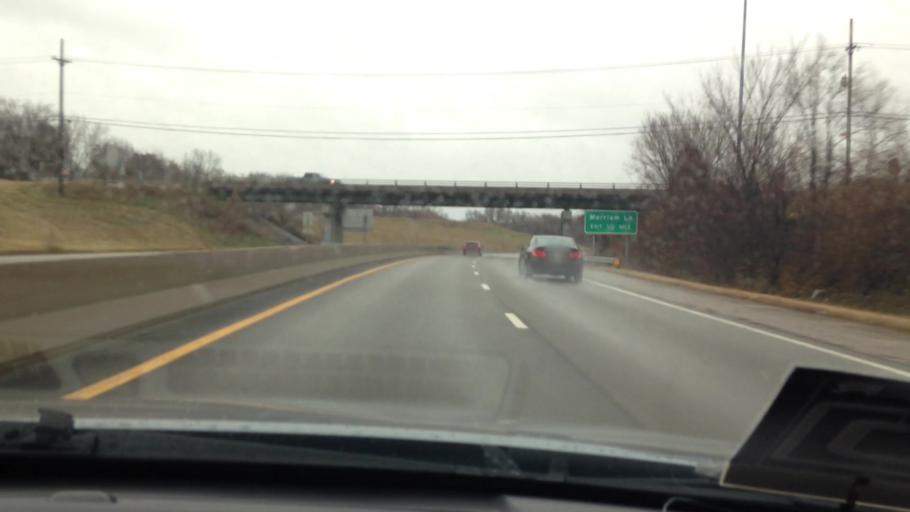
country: US
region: Kansas
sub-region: Johnson County
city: Roeland Park
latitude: 39.0632
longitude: -94.6473
